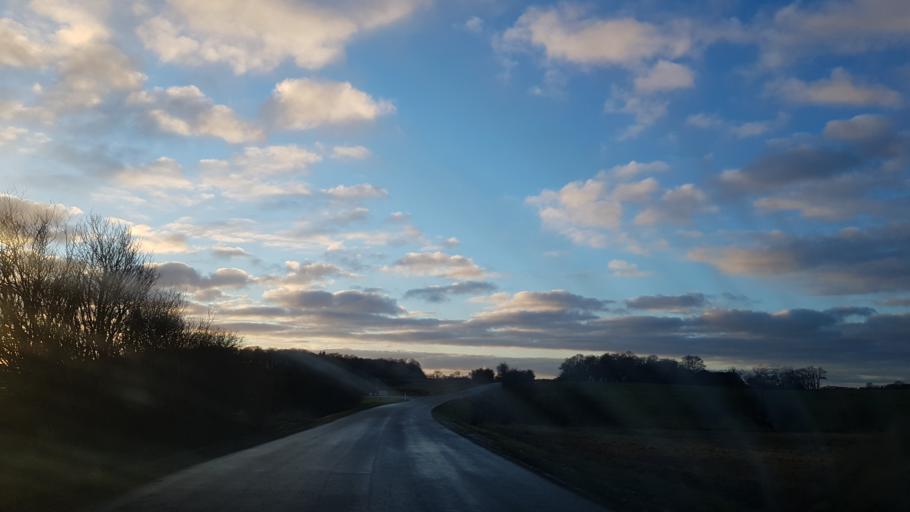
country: DK
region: South Denmark
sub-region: Kolding Kommune
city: Vamdrup
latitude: 55.3630
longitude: 9.3346
